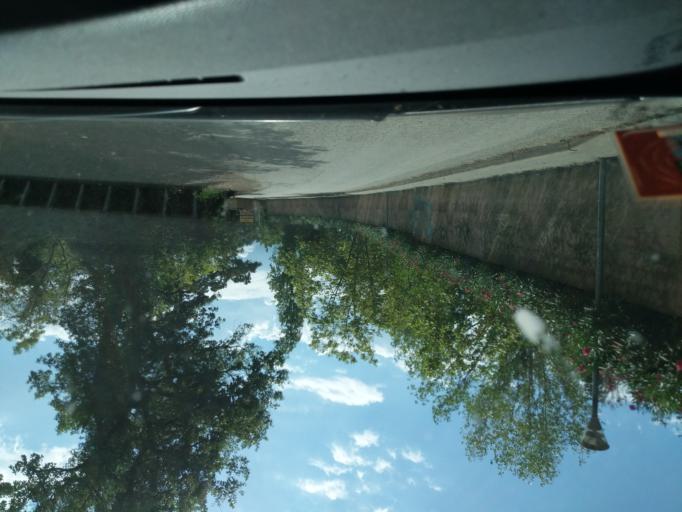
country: FR
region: Corsica
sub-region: Departement de la Haute-Corse
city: Ghisonaccia
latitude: 42.0003
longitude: 9.4440
